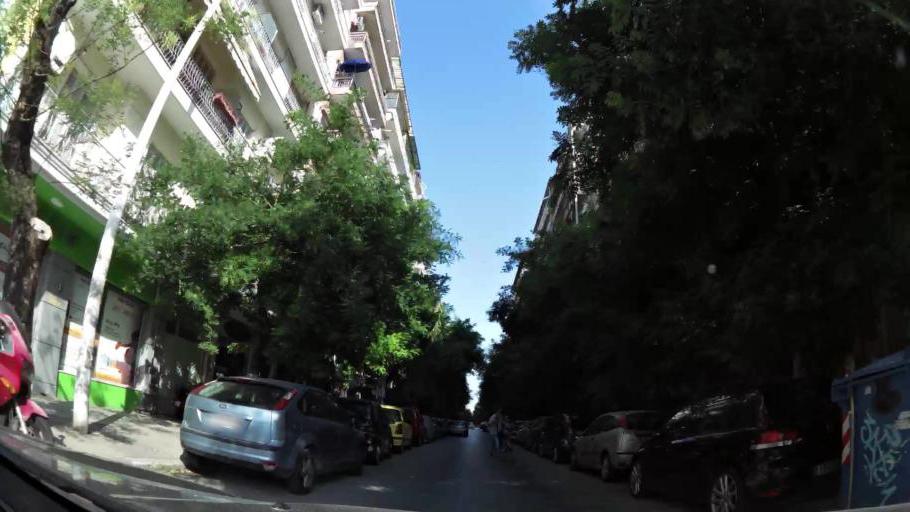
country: GR
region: Central Macedonia
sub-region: Nomos Thessalonikis
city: Sykies
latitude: 40.6400
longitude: 22.9430
